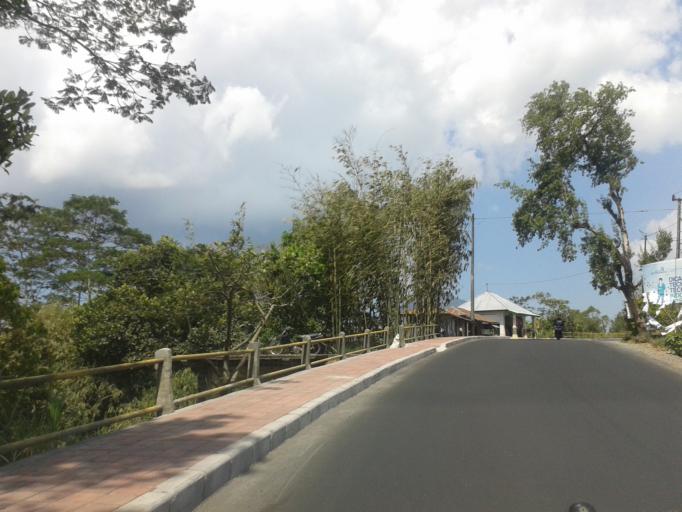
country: ID
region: Bali
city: Banjar Kedisan
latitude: -8.2782
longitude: 115.3545
